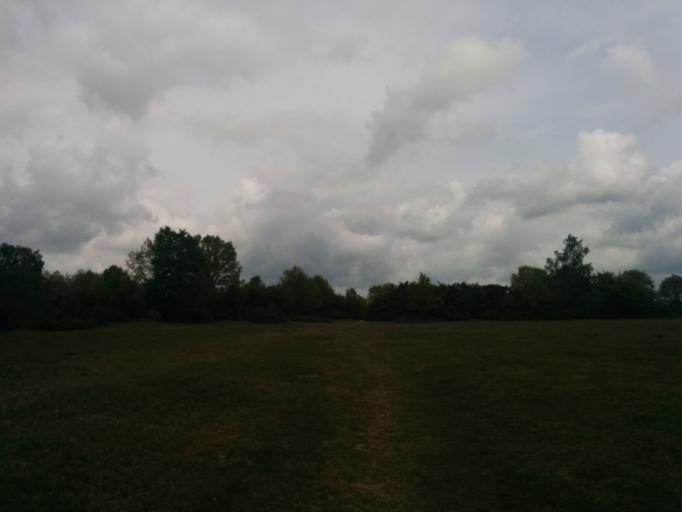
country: SE
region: Skane
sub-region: Lunds Kommun
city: Genarp
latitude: 55.5876
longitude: 13.3963
